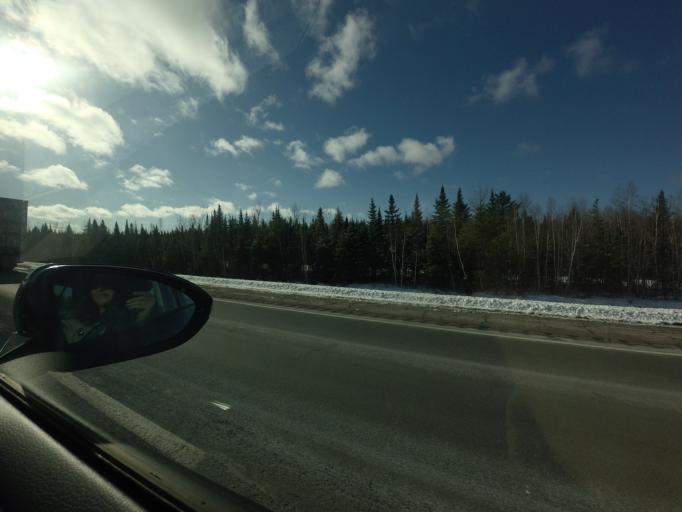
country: CA
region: New Brunswick
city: Fredericton
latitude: 45.8809
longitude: -66.6369
